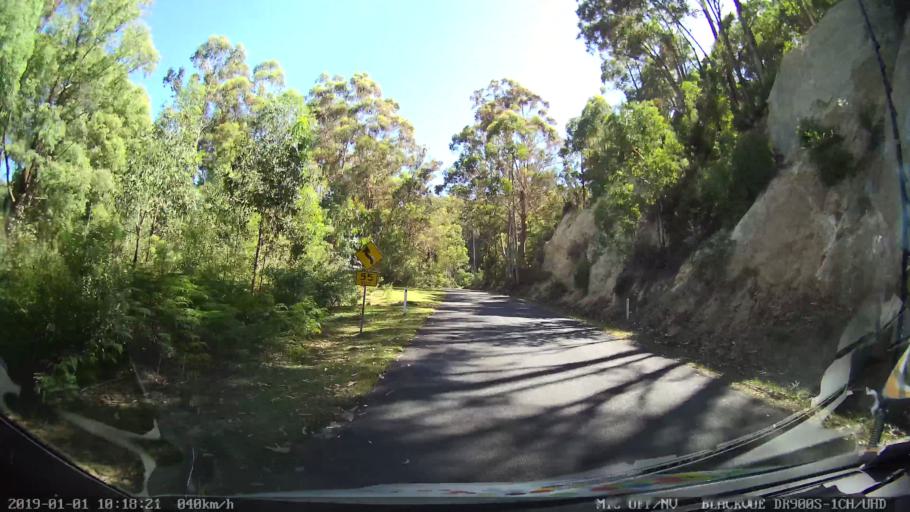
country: AU
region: New South Wales
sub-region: Snowy River
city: Jindabyne
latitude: -36.0891
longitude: 148.1816
